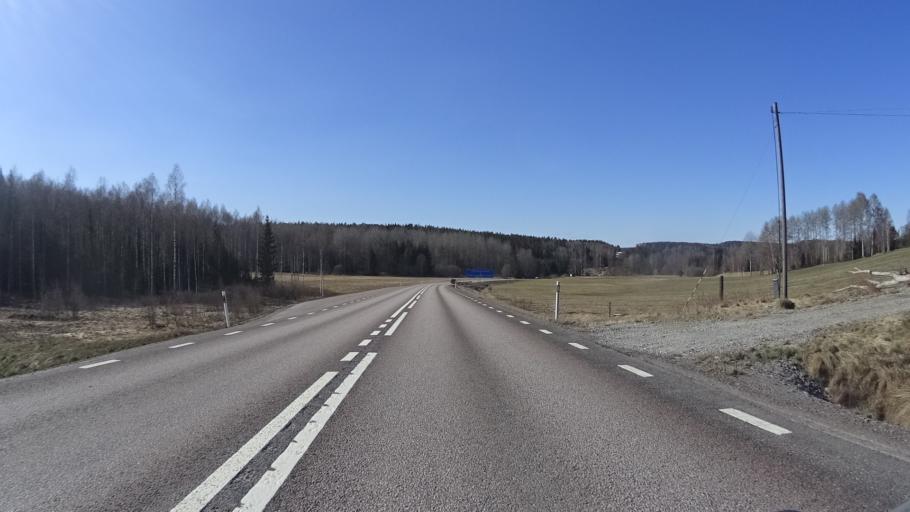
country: SE
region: Vaermland
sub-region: Karlstads Kommun
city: Edsvalla
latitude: 59.5298
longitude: 13.1195
